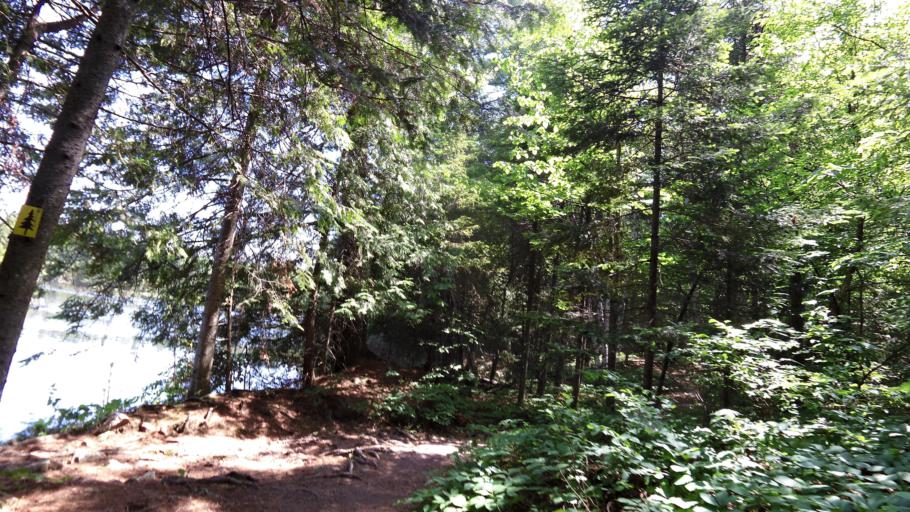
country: CA
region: Ontario
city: Arnprior
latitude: 45.4608
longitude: -76.2586
